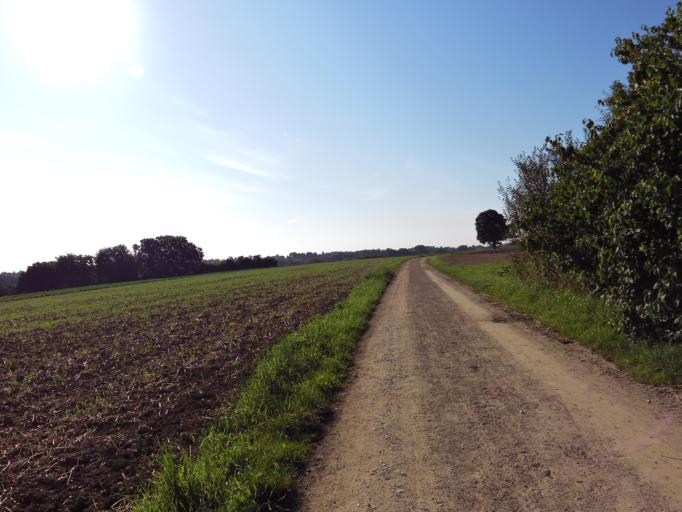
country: DE
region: North Rhine-Westphalia
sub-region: Regierungsbezirk Koln
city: Alsdorf
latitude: 50.8529
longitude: 6.1669
